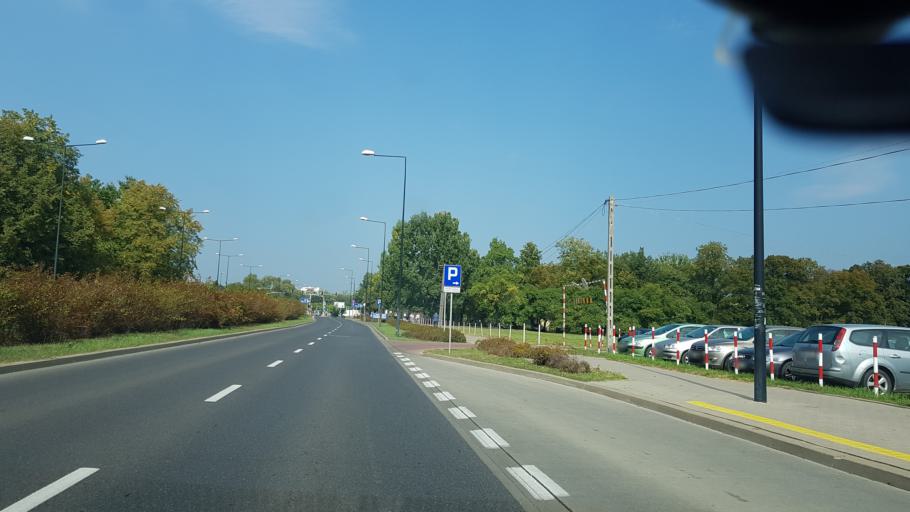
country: PL
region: Masovian Voivodeship
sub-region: Warszawa
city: Ursynow
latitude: 52.1614
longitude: 21.0492
